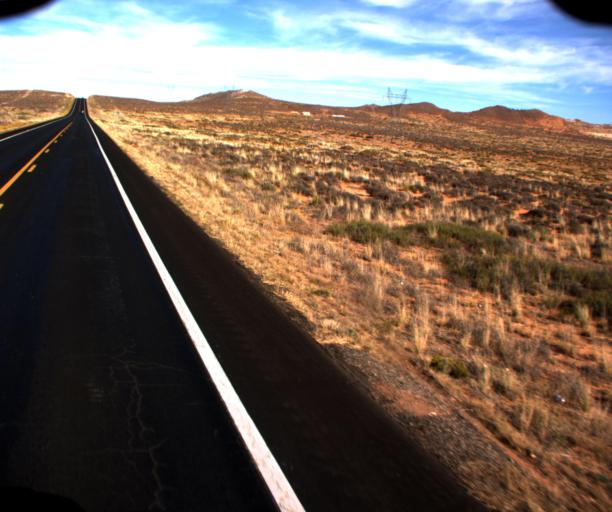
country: US
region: Arizona
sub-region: Apache County
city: Many Farms
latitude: 36.9485
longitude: -109.5237
